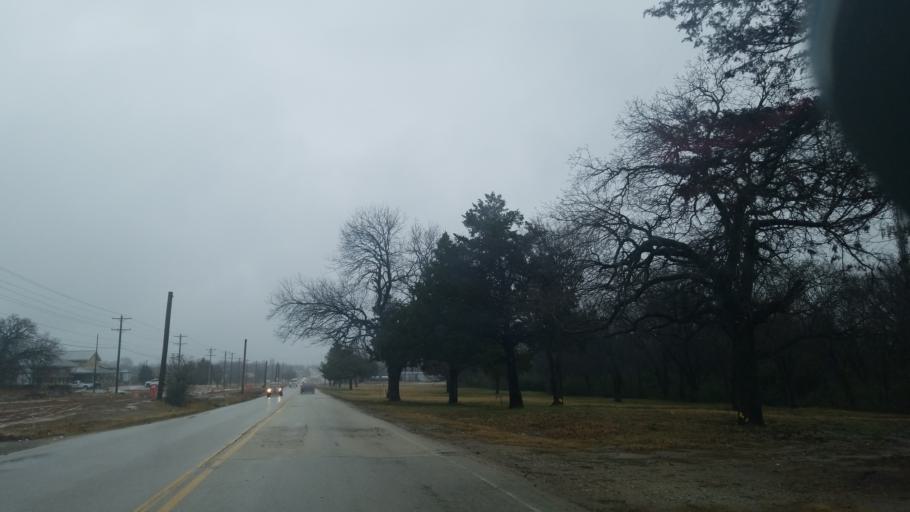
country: US
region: Texas
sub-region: Denton County
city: Corinth
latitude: 33.1998
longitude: -97.0845
